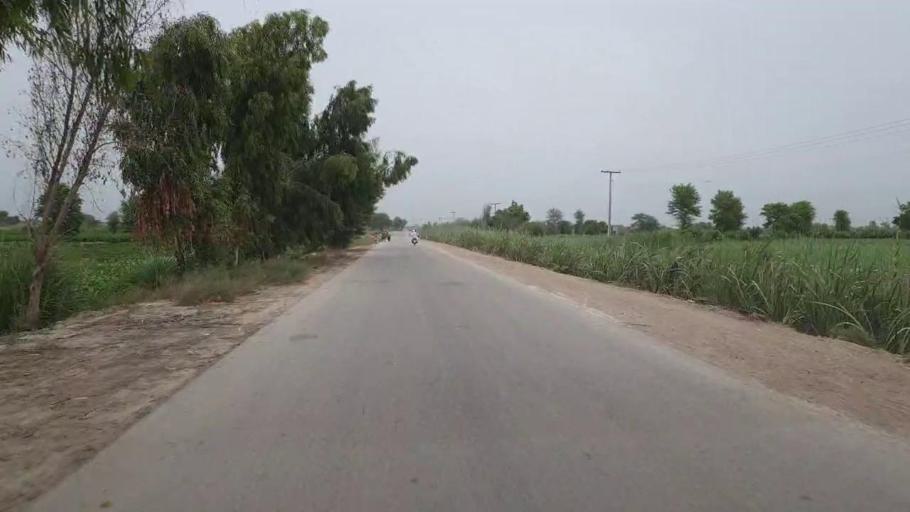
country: PK
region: Sindh
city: Bandhi
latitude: 26.5528
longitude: 68.2117
